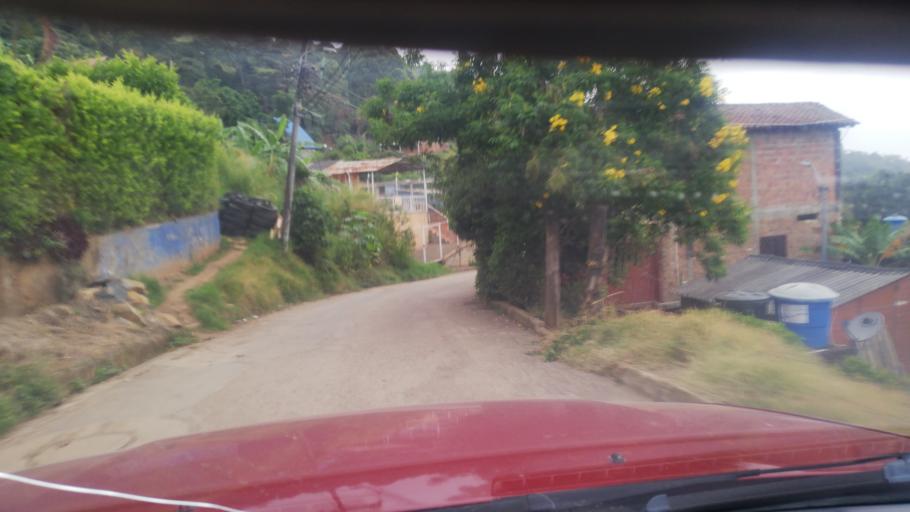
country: CO
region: Valle del Cauca
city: Cali
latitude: 3.5022
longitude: -76.5467
